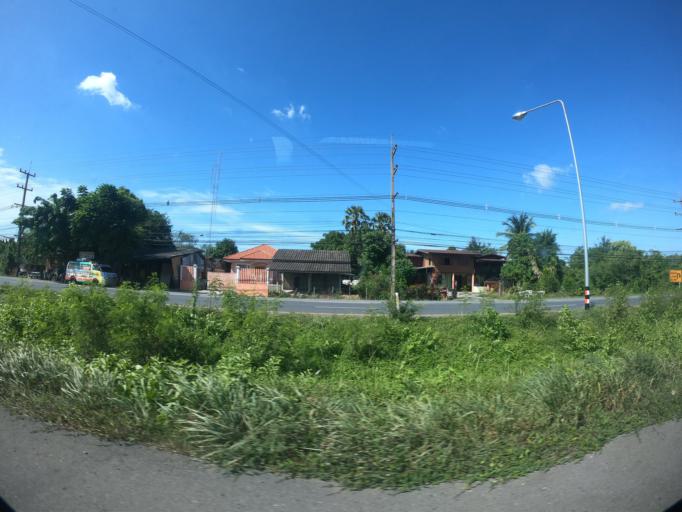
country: TH
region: Nakhon Nayok
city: Ban Na
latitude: 14.2546
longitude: 101.0893
